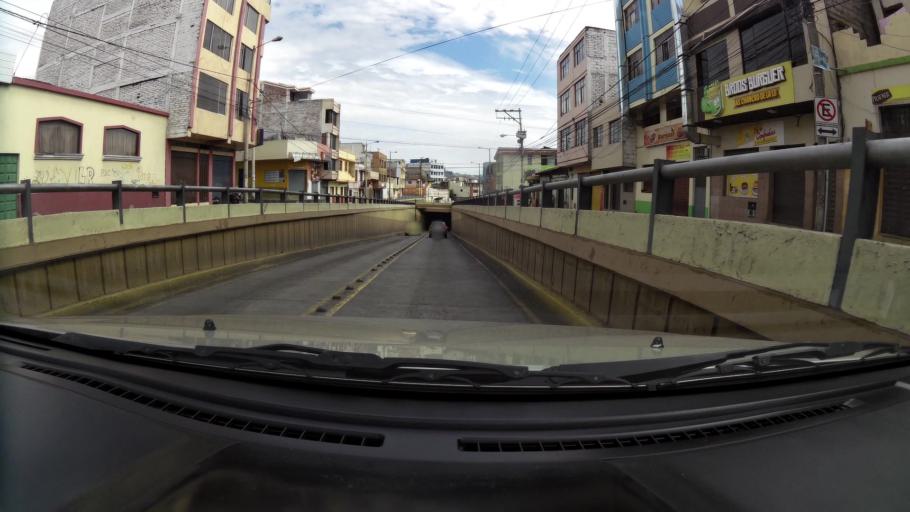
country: EC
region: Tungurahua
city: Ambato
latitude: -1.2486
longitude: -78.6324
